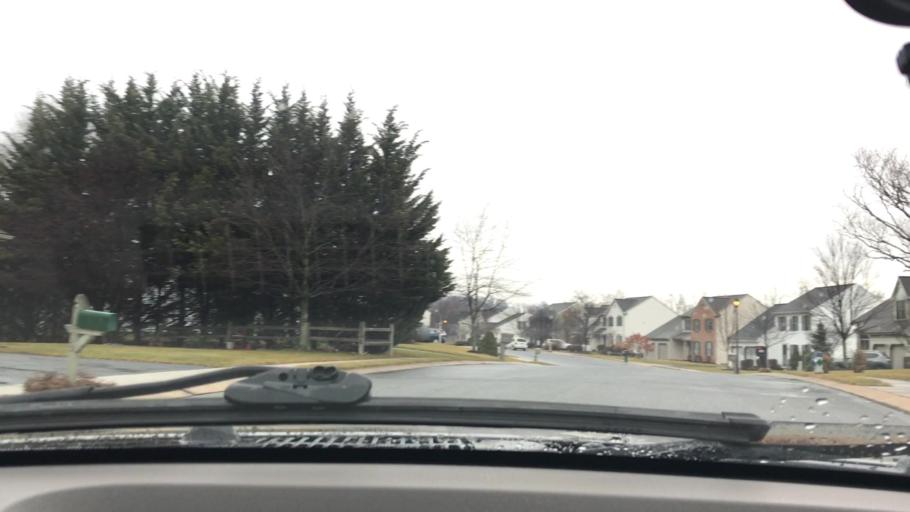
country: US
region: Pennsylvania
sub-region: Lancaster County
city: Elizabethtown
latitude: 40.1673
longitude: -76.5925
